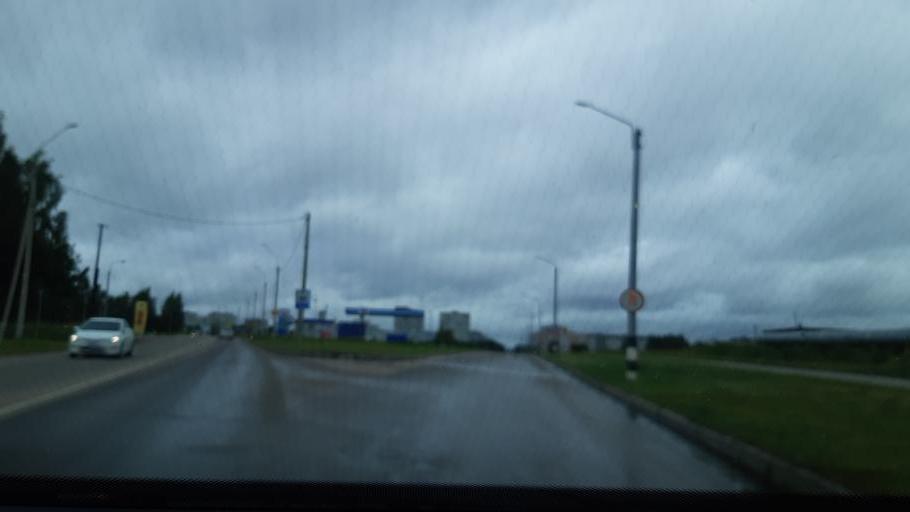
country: RU
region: Smolensk
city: Desnogorsk
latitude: 54.1410
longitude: 33.2785
